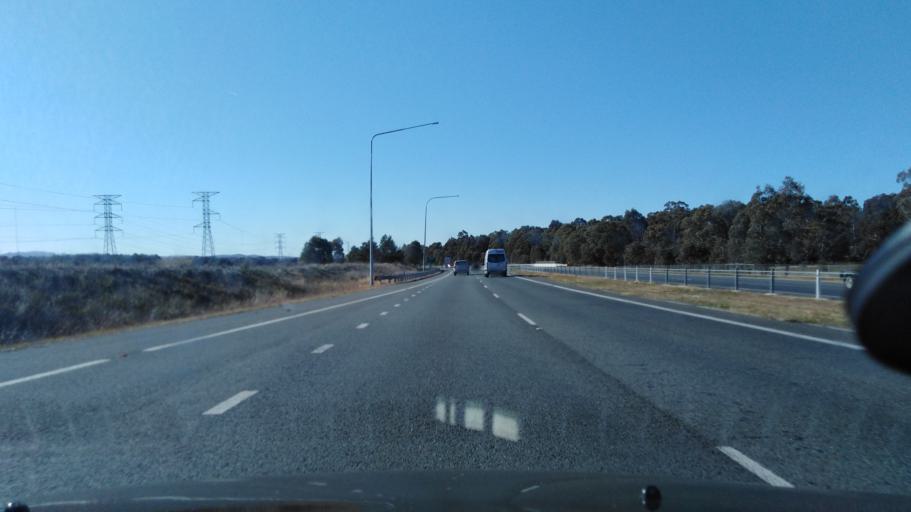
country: AU
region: Australian Capital Territory
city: Kaleen
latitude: -35.2382
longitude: 149.1131
